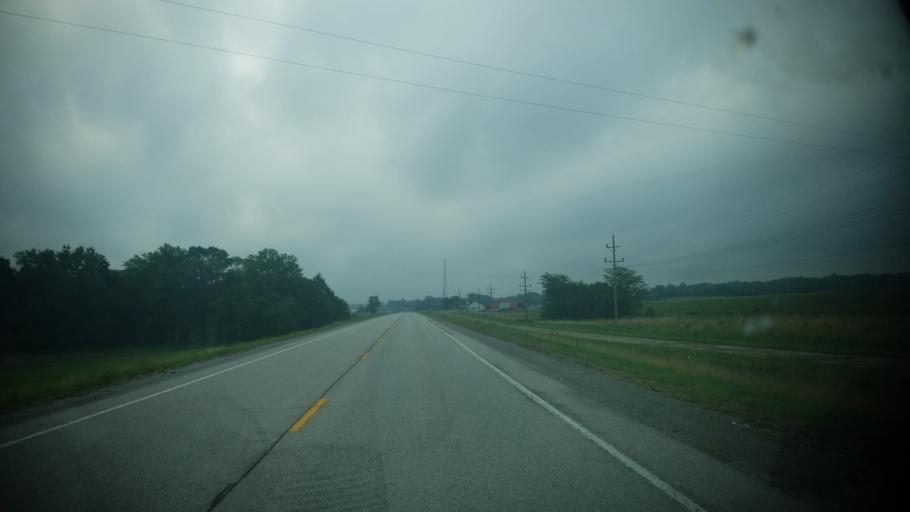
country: US
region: Illinois
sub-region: Clay County
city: Flora
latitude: 38.6779
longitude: -88.3718
